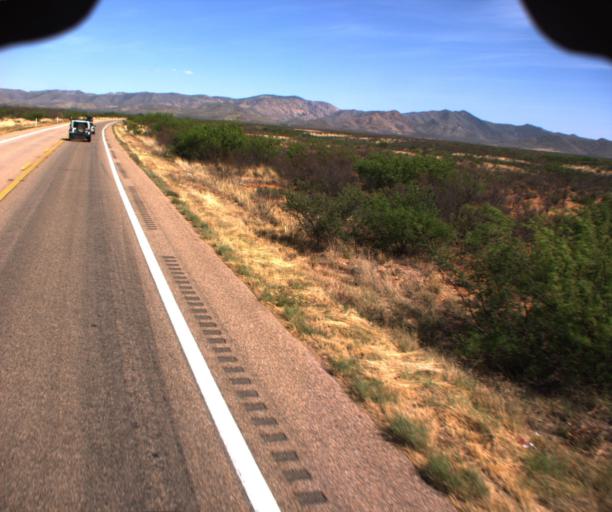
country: US
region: Arizona
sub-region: Cochise County
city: Sierra Vista Southeast
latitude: 31.5427
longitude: -110.0814
